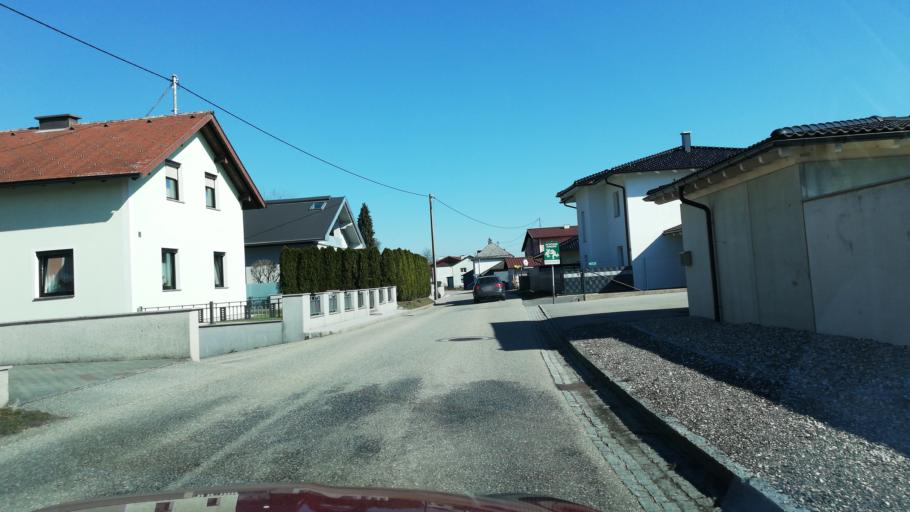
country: AT
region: Upper Austria
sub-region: Politischer Bezirk Vocklabruck
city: Redlham
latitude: 48.0330
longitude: 13.7374
